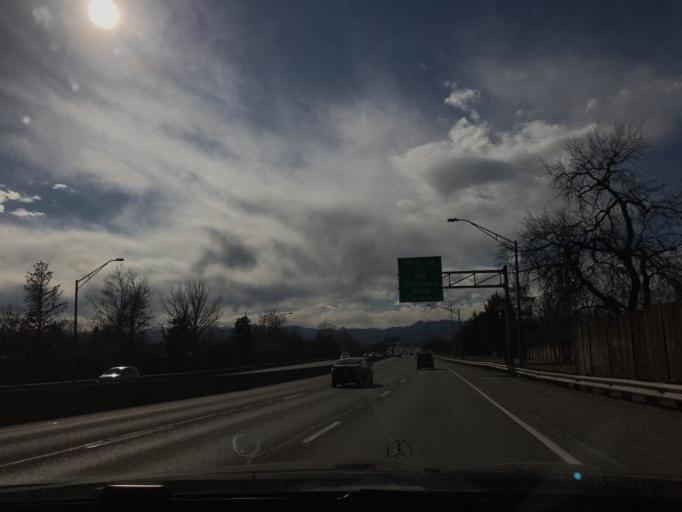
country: US
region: Colorado
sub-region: Adams County
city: Berkley
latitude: 39.7836
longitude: -105.0360
